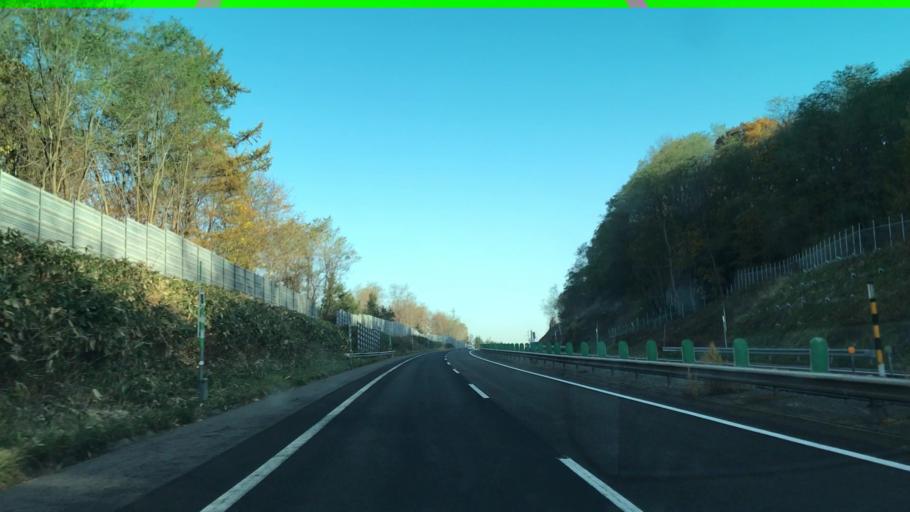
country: JP
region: Hokkaido
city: Sunagawa
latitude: 43.4194
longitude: 141.9110
